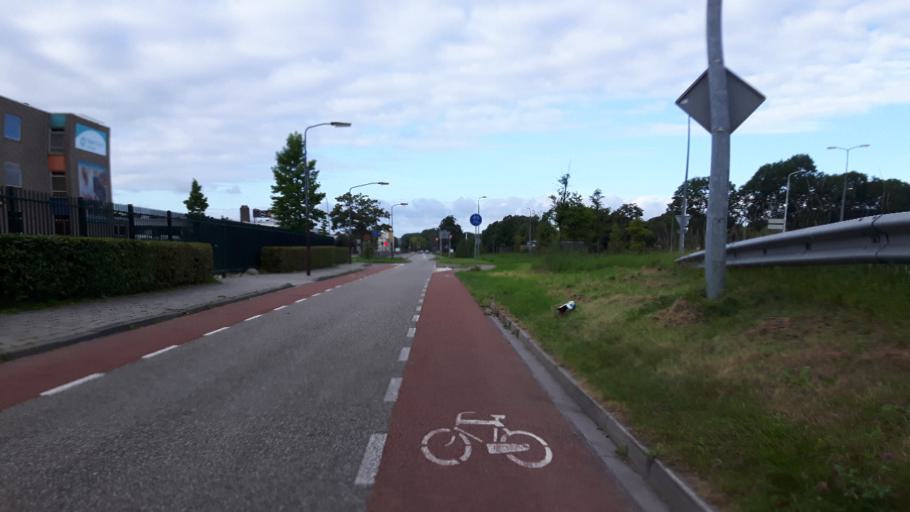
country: NL
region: North Holland
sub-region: Gemeente Hoorn
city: Hoorn
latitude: 52.6465
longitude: 5.0418
